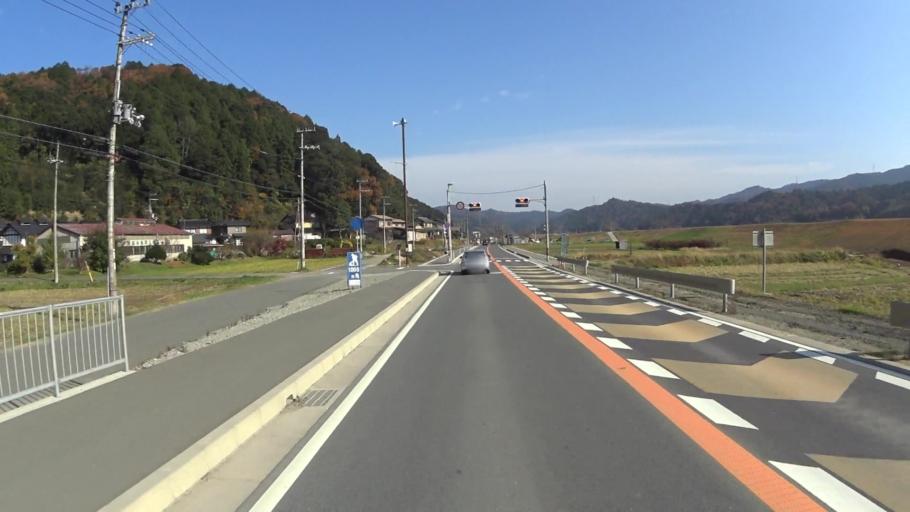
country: JP
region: Kyoto
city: Maizuru
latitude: 35.4265
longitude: 135.2414
